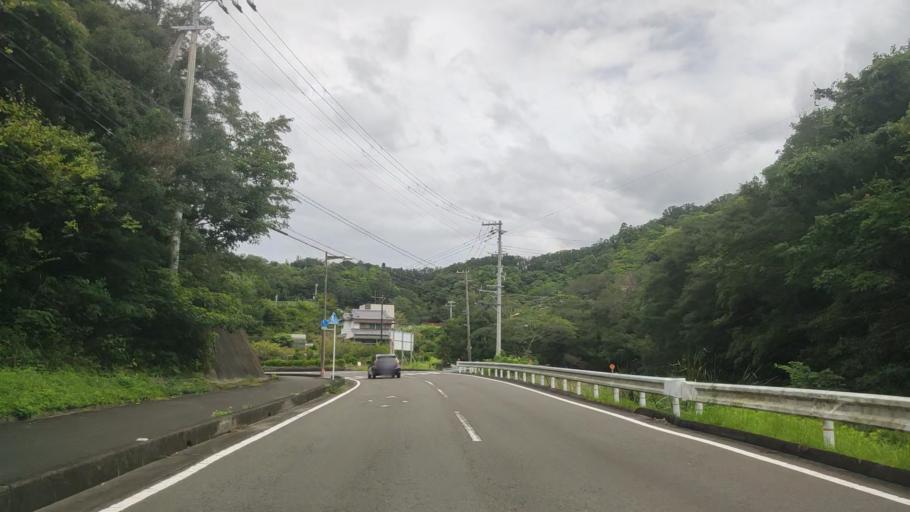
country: JP
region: Wakayama
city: Tanabe
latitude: 33.6820
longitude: 135.3889
